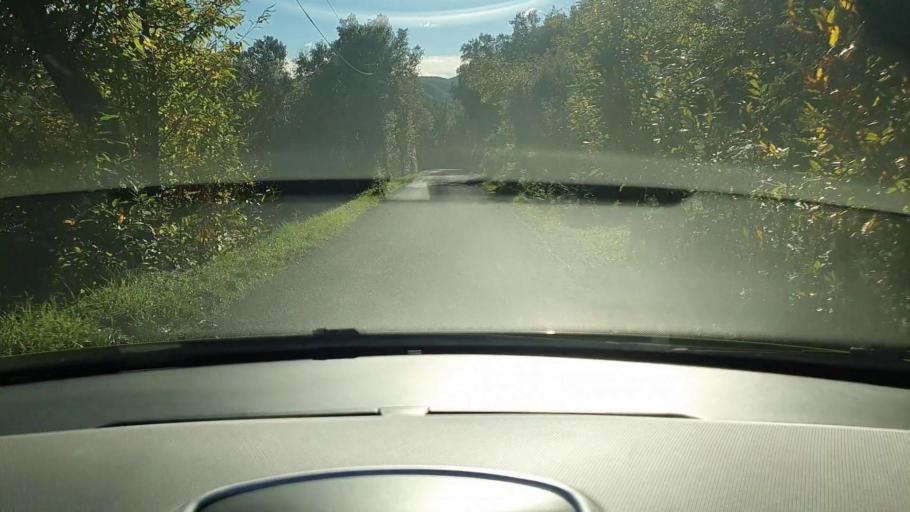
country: FR
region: Languedoc-Roussillon
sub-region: Departement du Gard
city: Le Vigan
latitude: 43.9957
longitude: 3.6280
